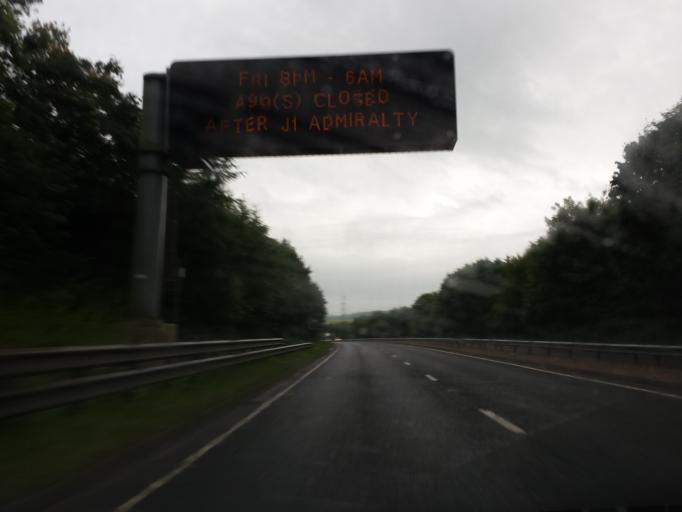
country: GB
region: Scotland
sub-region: Perth and Kinross
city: Perth
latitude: 56.3951
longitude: -3.4893
